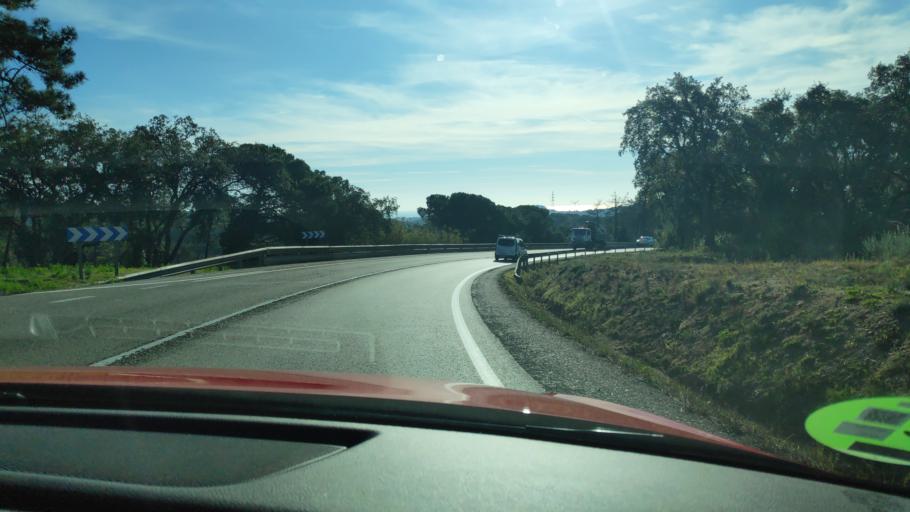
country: ES
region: Catalonia
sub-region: Provincia de Girona
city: Lloret de Mar
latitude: 41.7229
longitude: 2.8249
